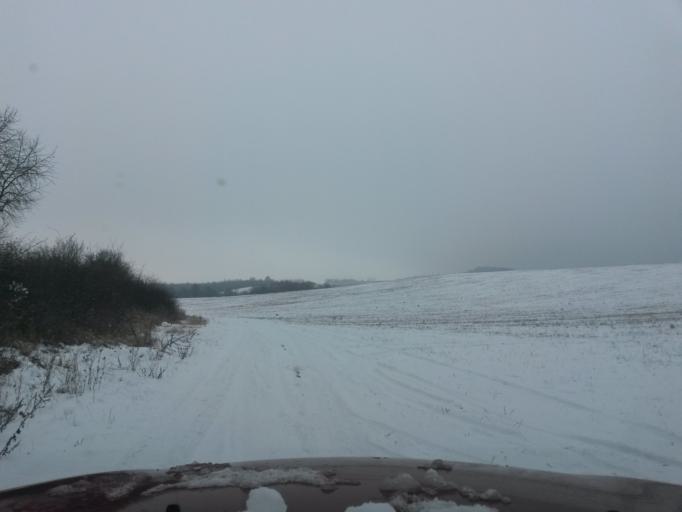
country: SK
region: Kosicky
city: Kosice
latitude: 48.7140
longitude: 21.3257
